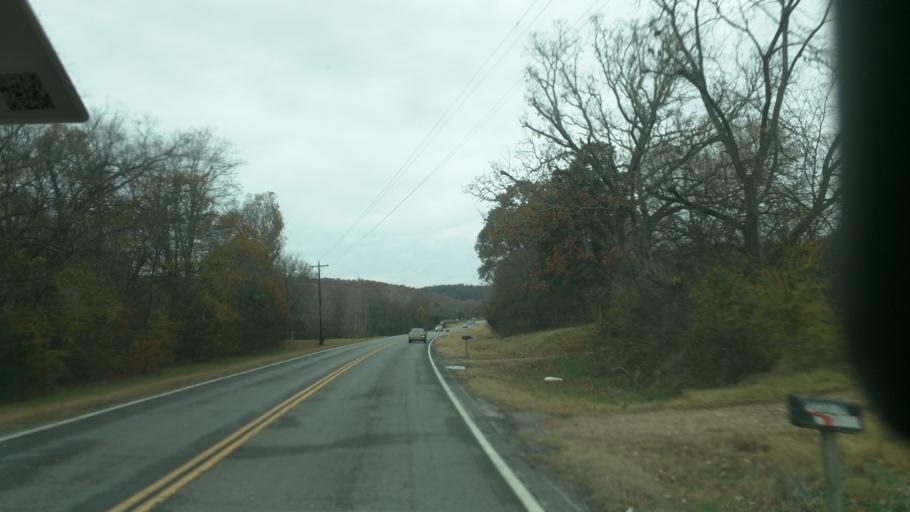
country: US
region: Oklahoma
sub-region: Cherokee County
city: Park Hill
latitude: 35.9111
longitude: -94.8328
